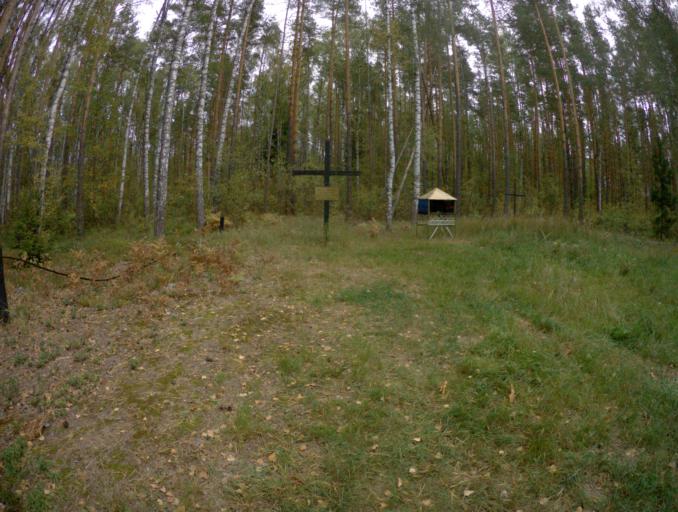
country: RU
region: Moskovskaya
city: Kerva
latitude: 55.7186
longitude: 39.5816
